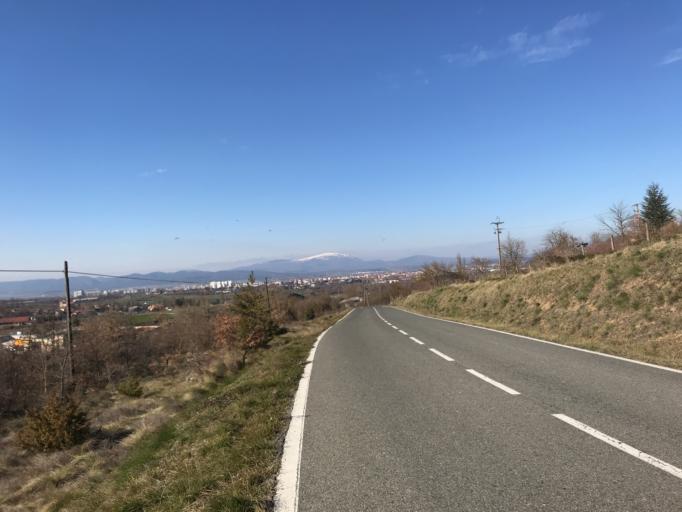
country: ES
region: Basque Country
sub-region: Provincia de Alava
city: Gasteiz / Vitoria
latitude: 42.8107
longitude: -2.6798
